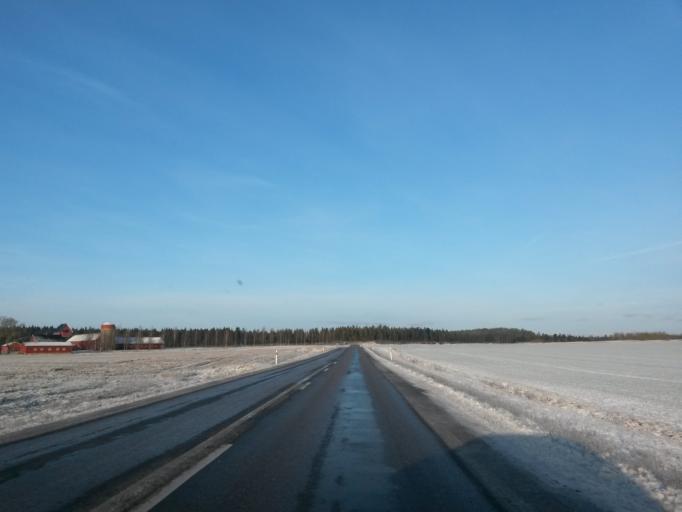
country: SE
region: Vaestra Goetaland
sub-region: Essunga Kommun
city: Nossebro
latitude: 58.0971
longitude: 12.6582
